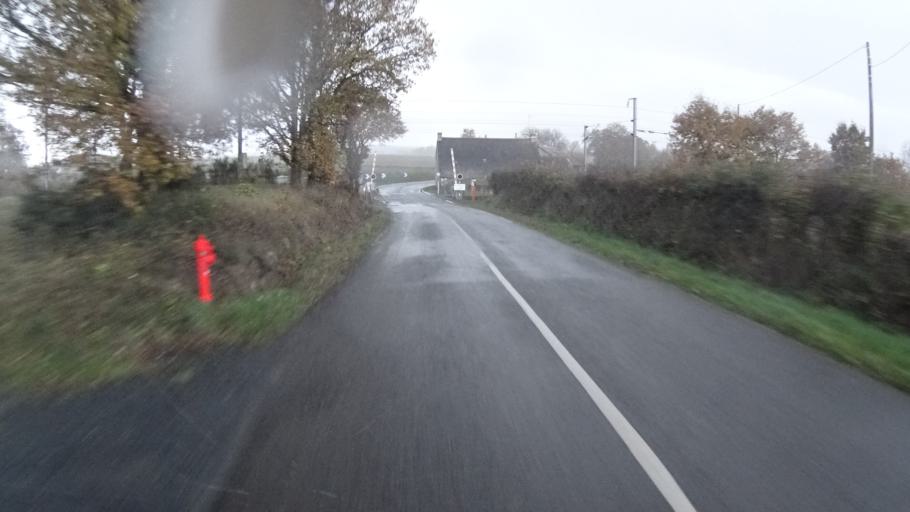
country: FR
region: Pays de la Loire
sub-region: Departement de la Loire-Atlantique
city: Avessac
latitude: 47.6674
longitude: -1.9860
